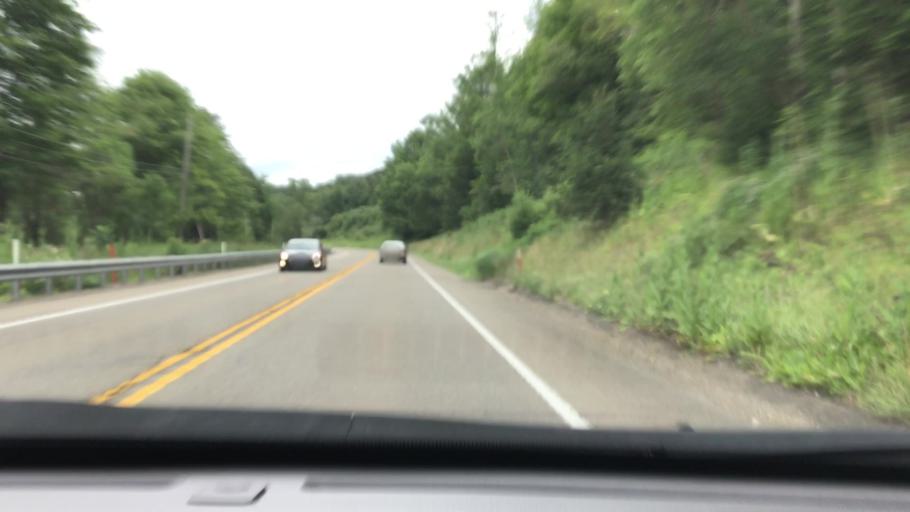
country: US
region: Pennsylvania
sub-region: Elk County
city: Johnsonburg
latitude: 41.5389
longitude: -78.6821
